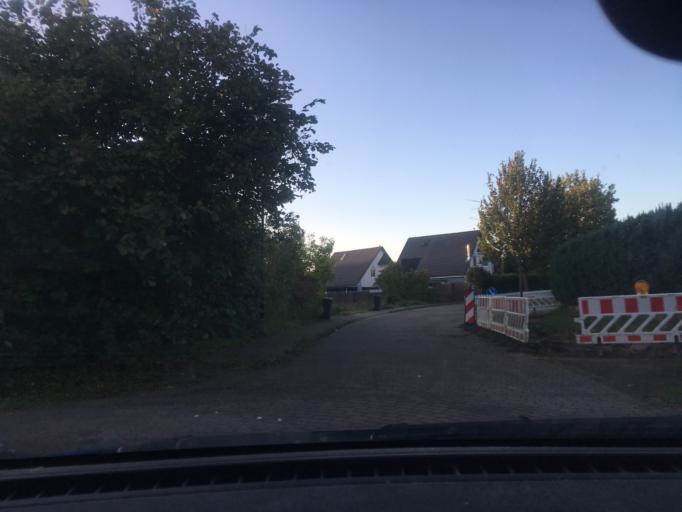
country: DE
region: Lower Saxony
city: Deutsch Evern
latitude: 53.2009
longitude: 10.4356
